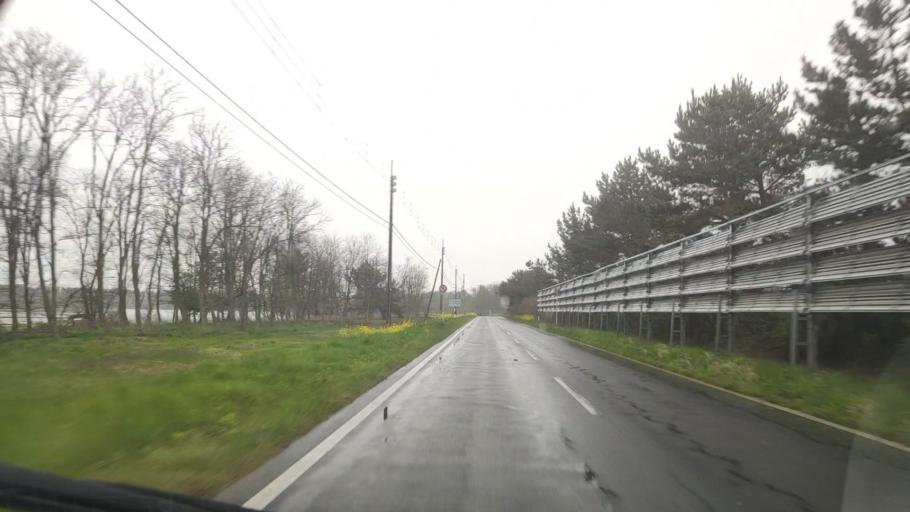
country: JP
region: Akita
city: Tenno
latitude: 40.0384
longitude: 139.9545
